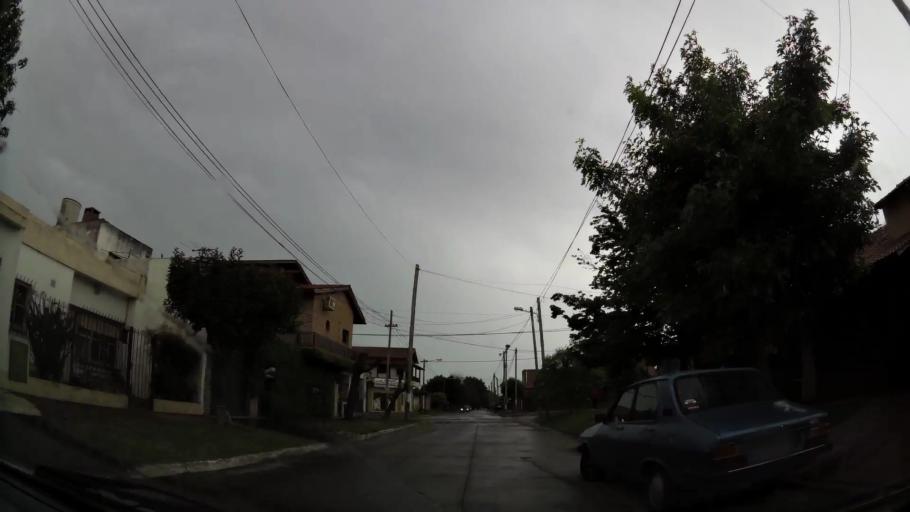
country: AR
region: Buenos Aires
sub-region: Partido de Quilmes
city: Quilmes
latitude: -34.7729
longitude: -58.2202
